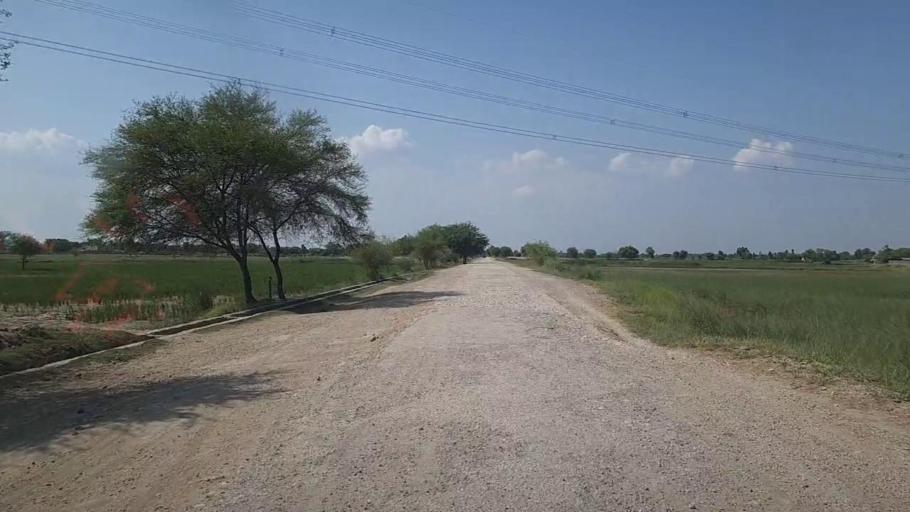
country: PK
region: Sindh
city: Khairpur
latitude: 28.1086
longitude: 69.6216
